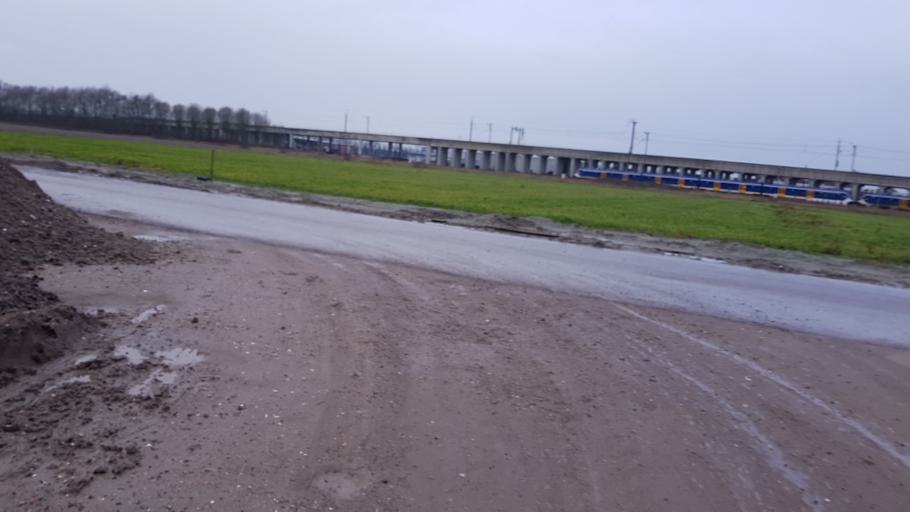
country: NL
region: North Holland
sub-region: Gemeente Haarlemmermeer
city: Hoofddorp
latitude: 52.2873
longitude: 4.6928
